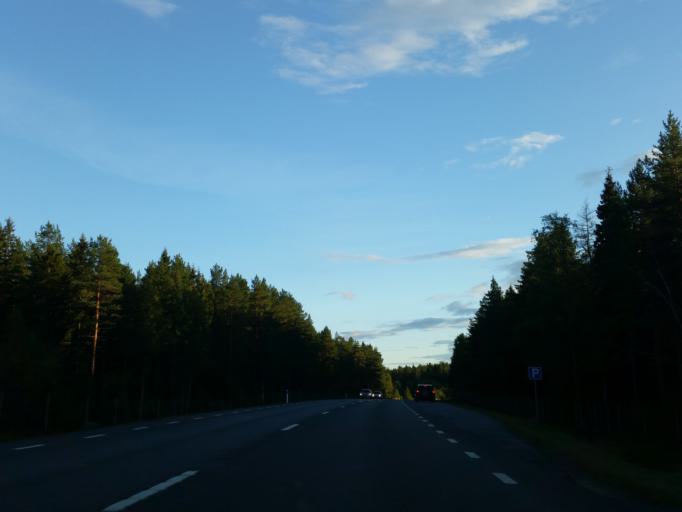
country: SE
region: Vaesterbotten
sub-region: Robertsfors Kommun
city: Robertsfors
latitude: 64.0249
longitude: 20.8410
